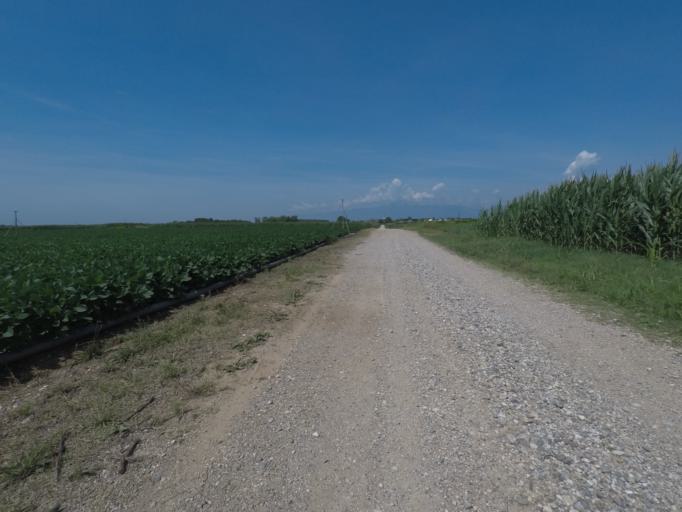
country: IT
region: Friuli Venezia Giulia
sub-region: Provincia di Udine
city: Dignano
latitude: 46.0835
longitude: 12.9550
